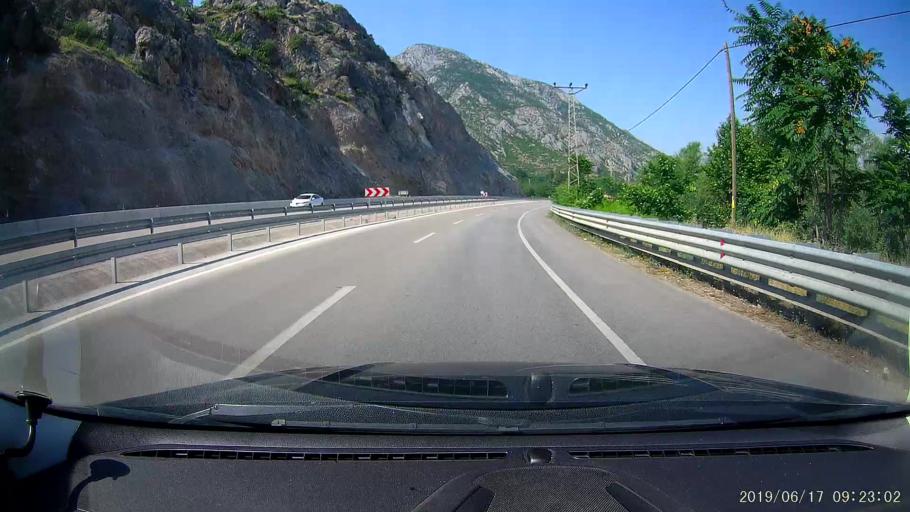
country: TR
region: Amasya
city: Amasya
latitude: 40.6799
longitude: 35.8818
